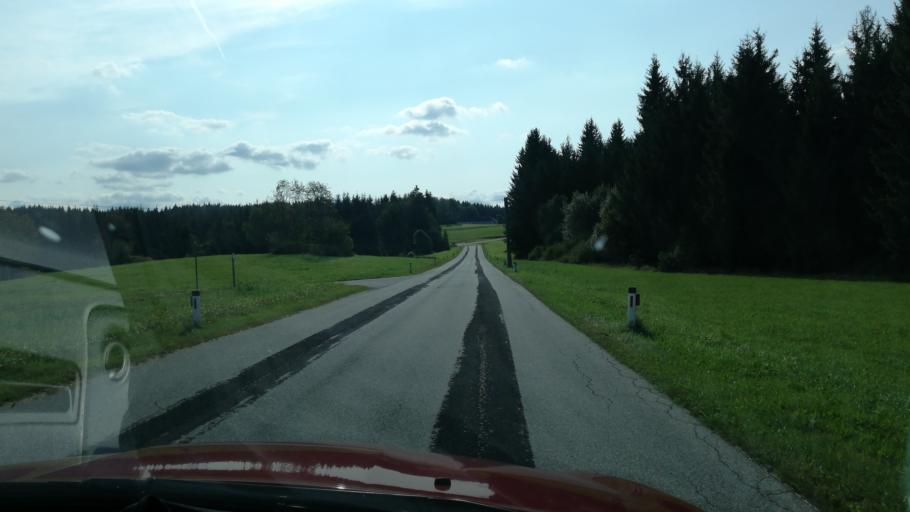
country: AT
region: Lower Austria
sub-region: Politischer Bezirk Zwettl
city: Langschlag
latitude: 48.5095
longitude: 14.8387
